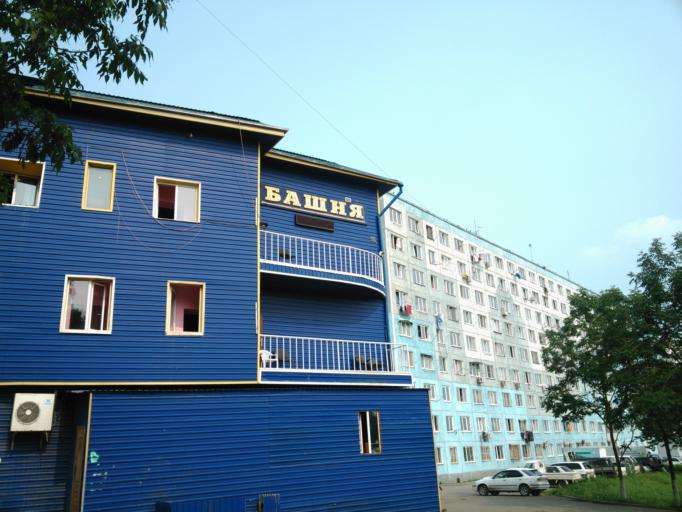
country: RU
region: Primorskiy
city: Vladivostok
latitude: 43.0929
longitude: 131.9759
